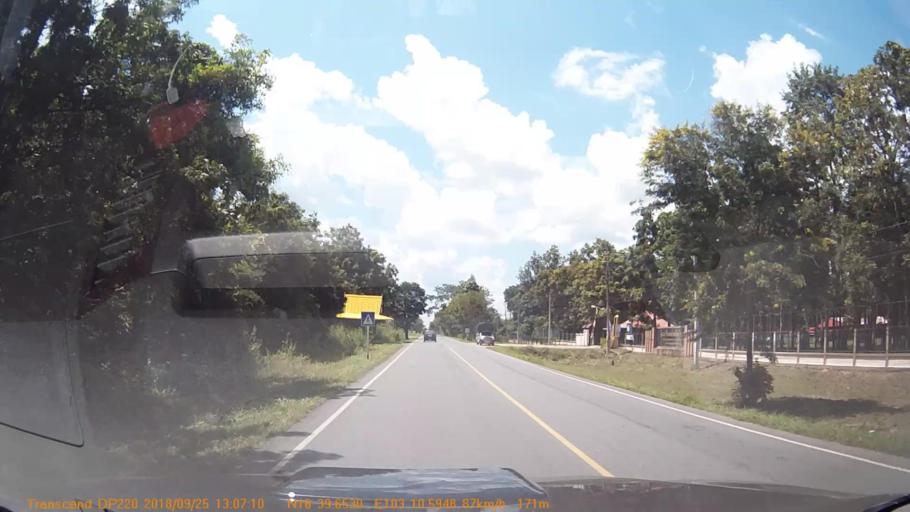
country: TH
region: Kalasin
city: Huai Mek
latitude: 16.6609
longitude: 103.1764
